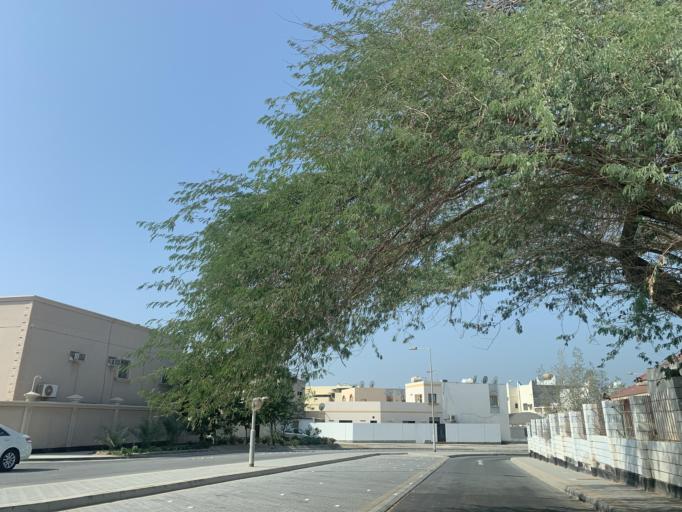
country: BH
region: Central Governorate
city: Madinat Hamad
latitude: 26.1271
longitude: 50.5022
